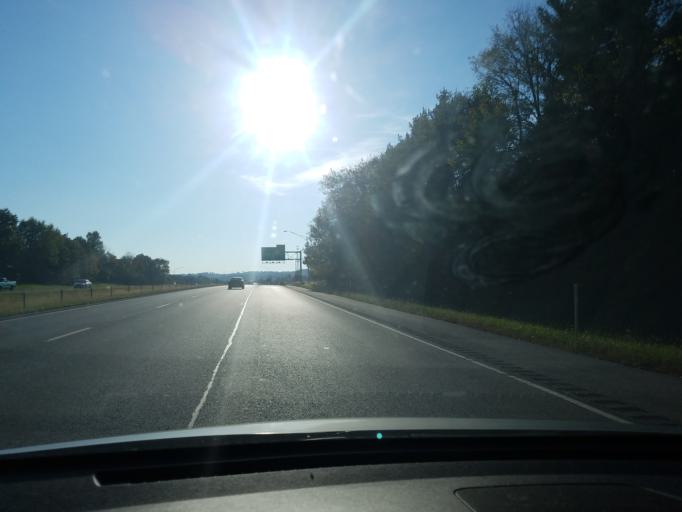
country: US
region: Indiana
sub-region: Floyd County
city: New Albany
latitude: 38.3394
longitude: -85.8122
